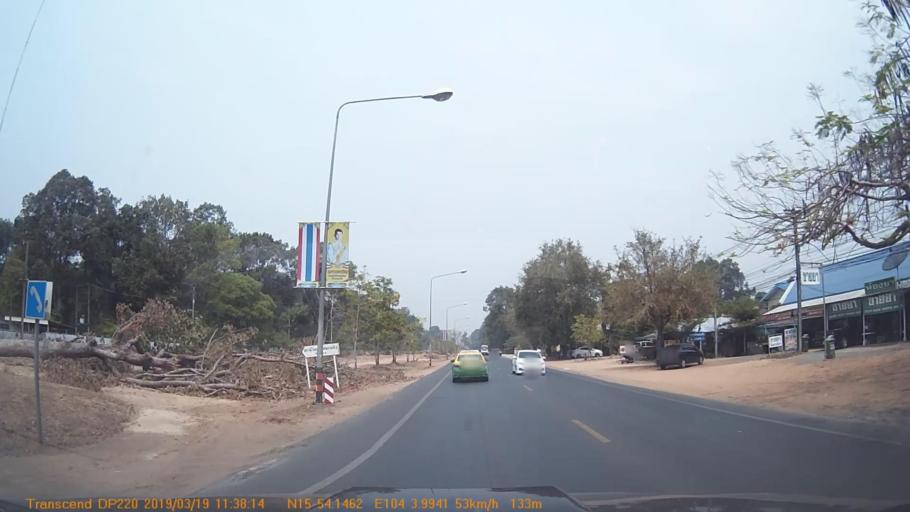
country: TH
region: Yasothon
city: Yasothon
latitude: 15.9025
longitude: 104.0665
